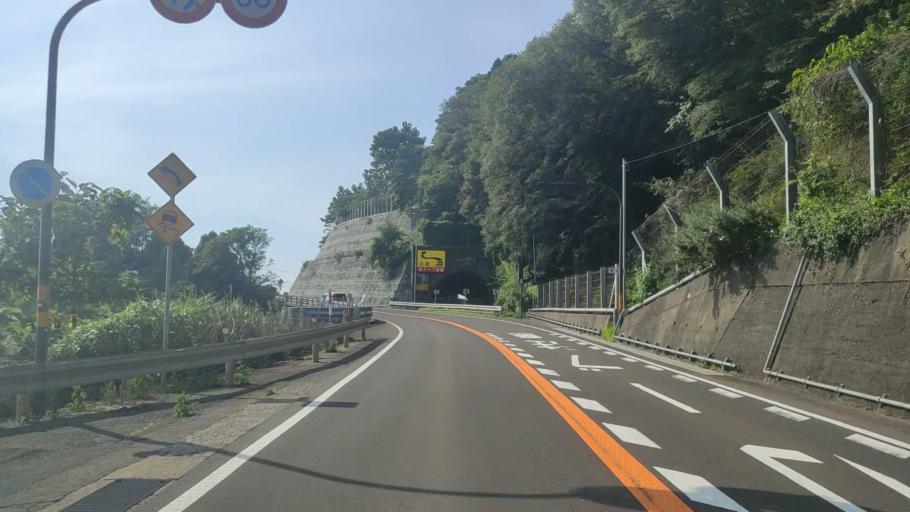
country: JP
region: Fukui
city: Takefu
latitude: 35.7916
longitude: 136.0942
